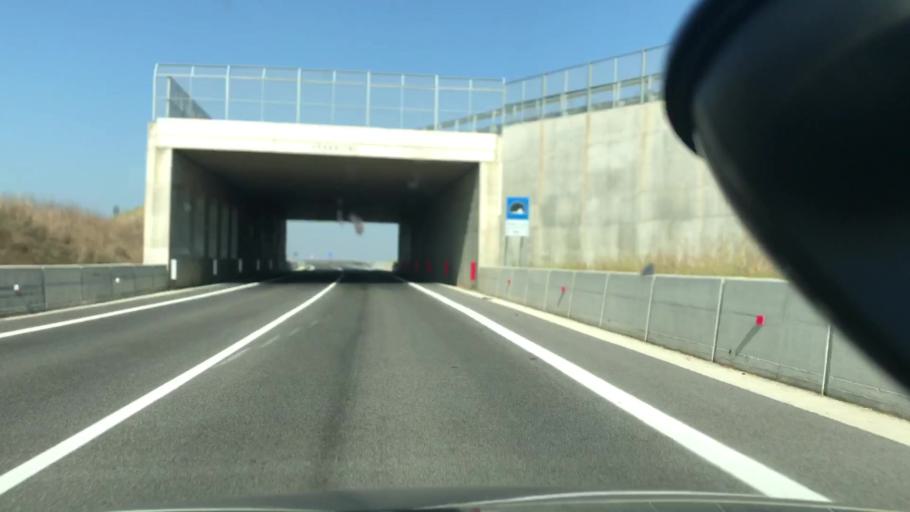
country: IT
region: Basilicate
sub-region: Provincia di Potenza
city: Palazzo San Gervasio
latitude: 40.9690
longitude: 16.0028
